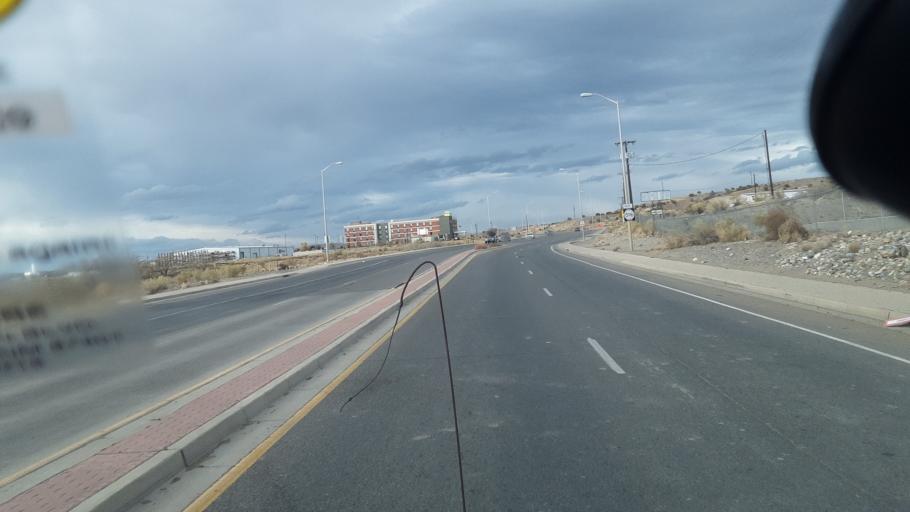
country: US
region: New Mexico
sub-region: San Juan County
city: Farmington
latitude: 36.7194
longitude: -108.1573
